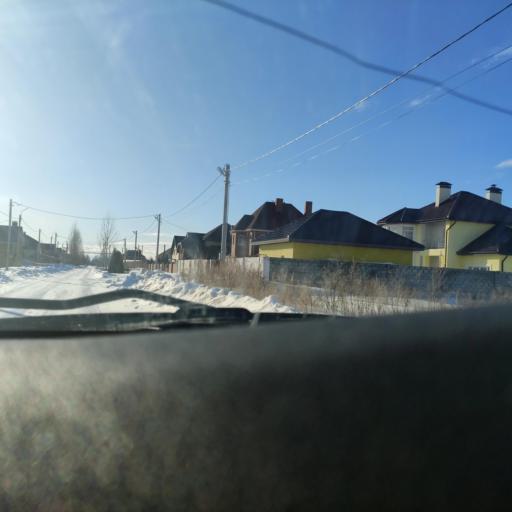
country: RU
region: Samara
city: Podstepki
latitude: 53.5101
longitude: 49.1677
